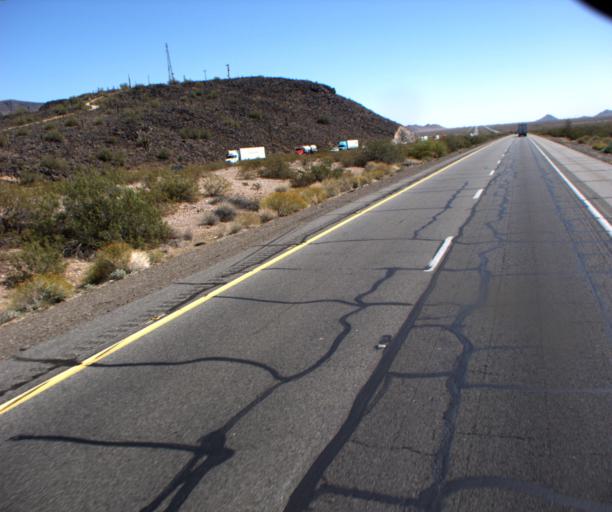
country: US
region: Arizona
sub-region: La Paz County
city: Salome
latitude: 33.5292
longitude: -113.1193
